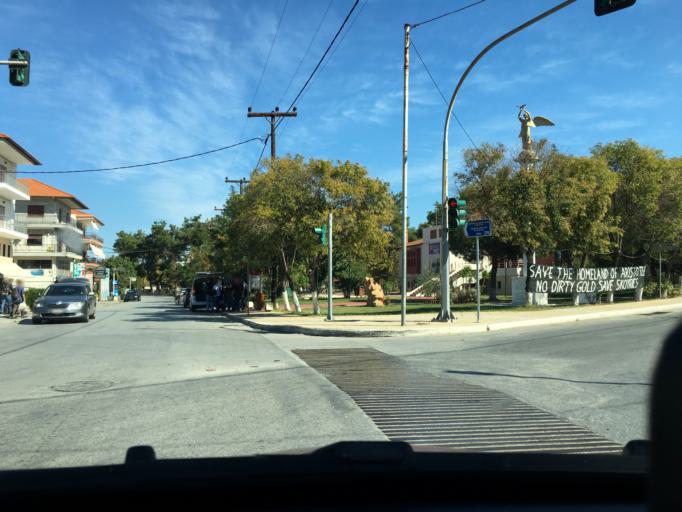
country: GR
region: Central Macedonia
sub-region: Nomos Chalkidikis
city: Ierissos
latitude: 40.3971
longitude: 23.8760
